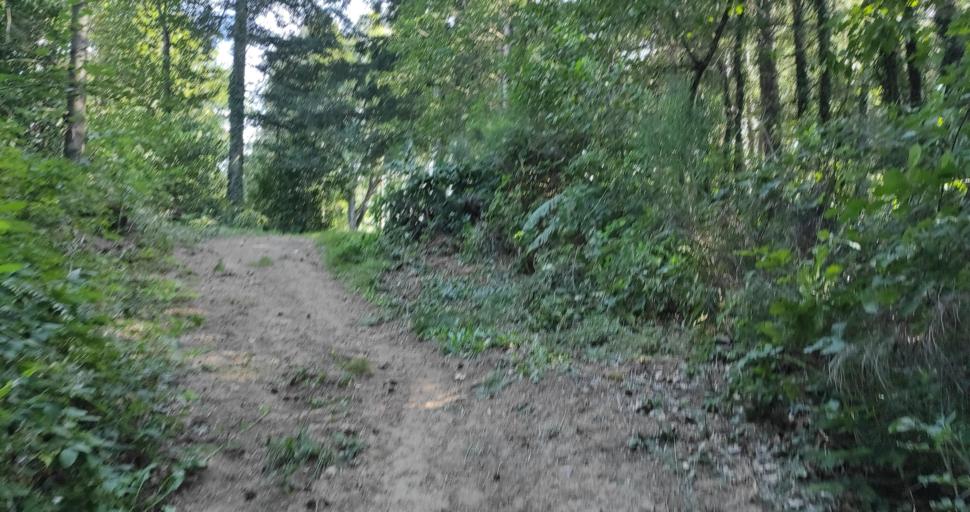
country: FR
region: Midi-Pyrenees
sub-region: Departement de l'Aveyron
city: La Loubiere
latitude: 44.3763
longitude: 2.7037
